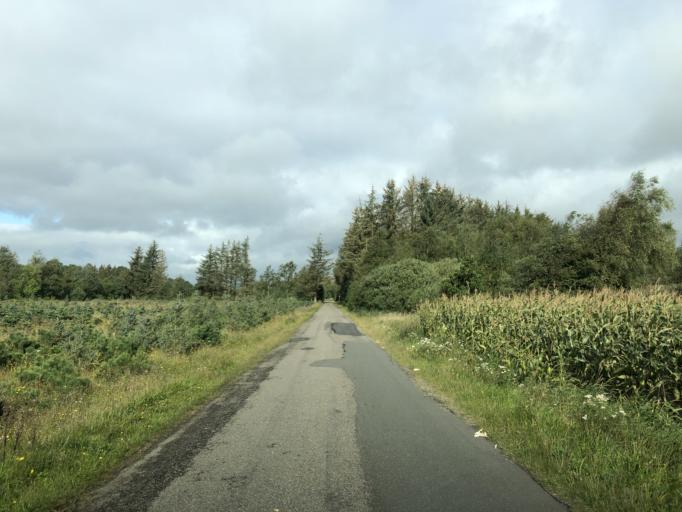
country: DK
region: Central Jutland
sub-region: Holstebro Kommune
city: Ulfborg
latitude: 56.2948
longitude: 8.4530
